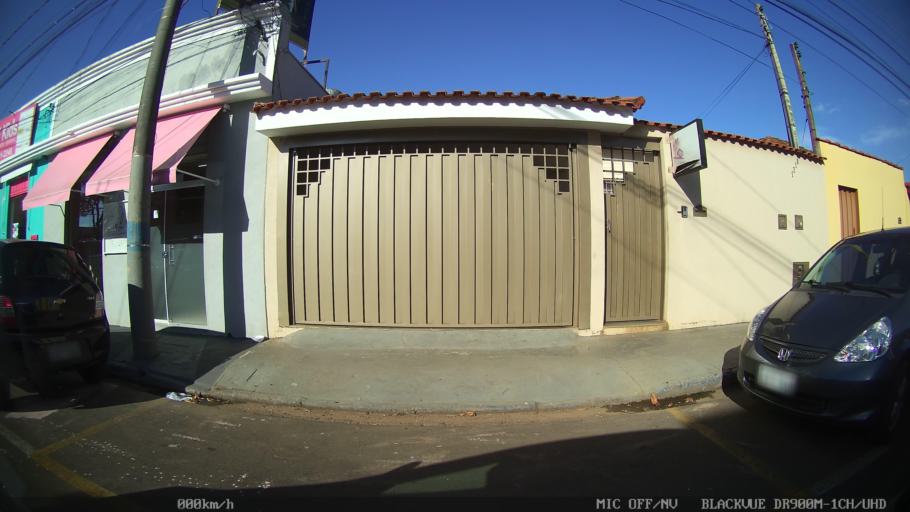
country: BR
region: Sao Paulo
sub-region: Franca
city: Franca
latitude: -20.5315
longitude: -47.4160
